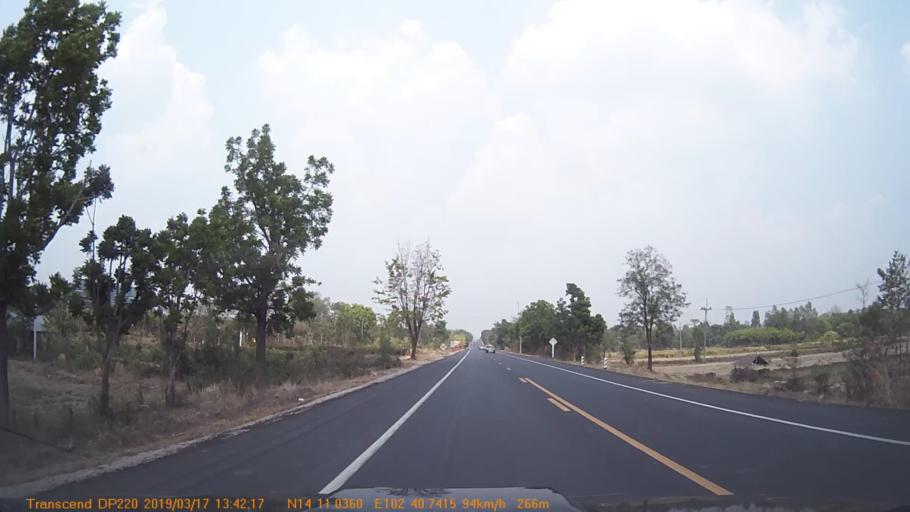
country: TH
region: Buriram
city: Non Din Daeng
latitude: 14.1840
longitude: 102.6792
